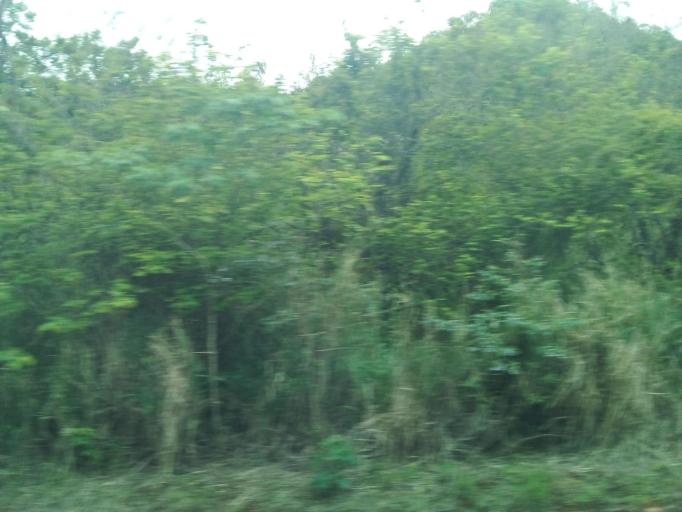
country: BR
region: Minas Gerais
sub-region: Rio Piracicaba
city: Rio Piracicaba
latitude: -19.9719
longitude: -43.2410
